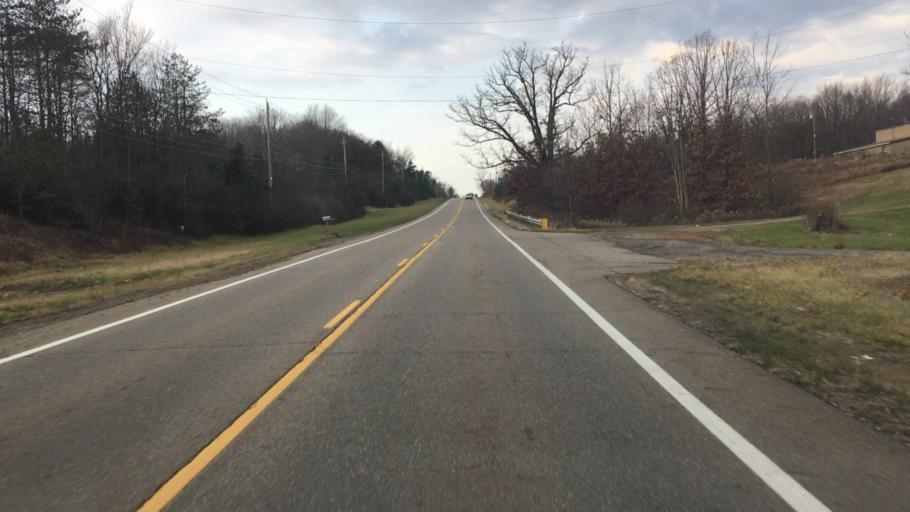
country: US
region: Ohio
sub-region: Mahoning County
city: Canfield
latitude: 41.0245
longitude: -80.8426
